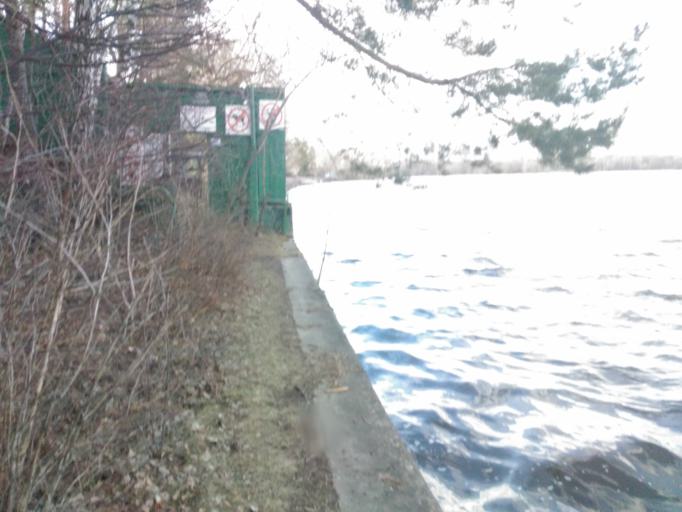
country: RU
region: Moscow
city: Shchukino
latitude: 55.7870
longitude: 37.4208
